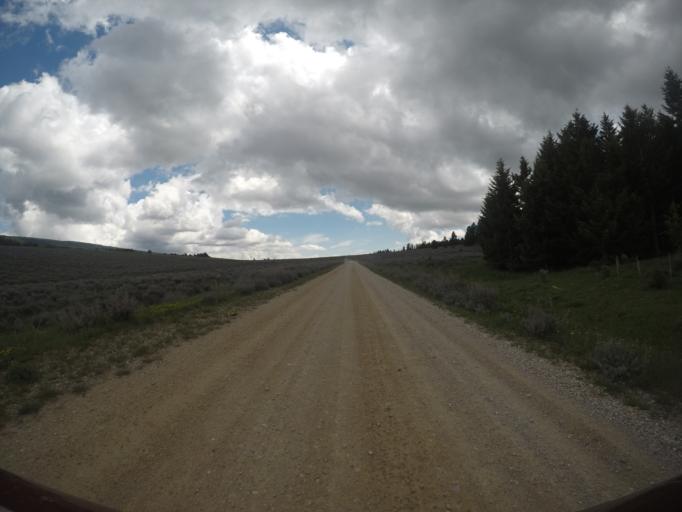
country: US
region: Wyoming
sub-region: Big Horn County
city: Lovell
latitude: 45.1731
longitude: -108.4556
